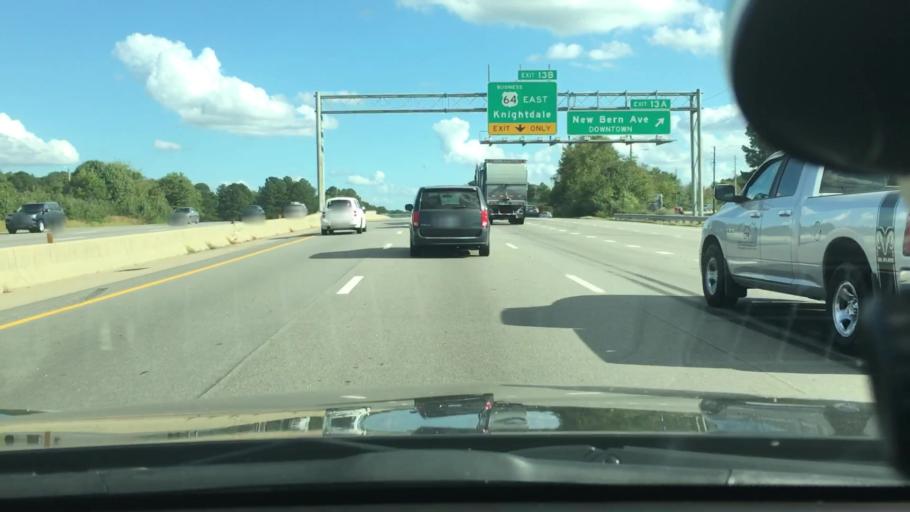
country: US
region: North Carolina
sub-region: Wake County
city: Raleigh
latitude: 35.7971
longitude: -78.5865
